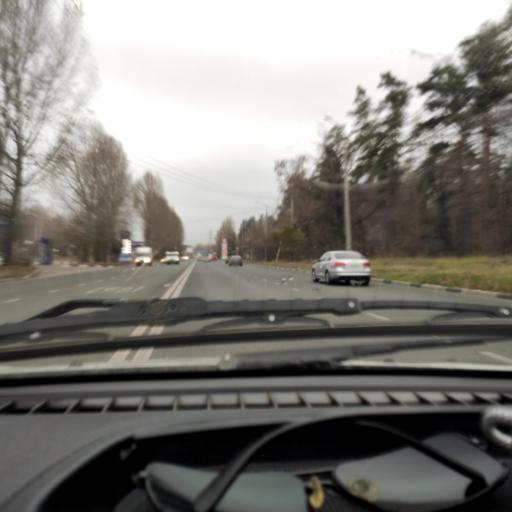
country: RU
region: Samara
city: Zhigulevsk
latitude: 53.5069
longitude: 49.4653
